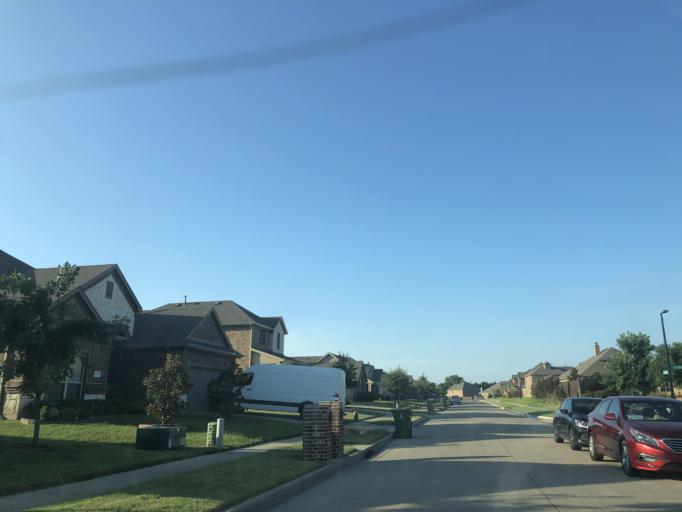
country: US
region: Texas
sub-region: Dallas County
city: Sunnyvale
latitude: 32.8459
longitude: -96.5567
